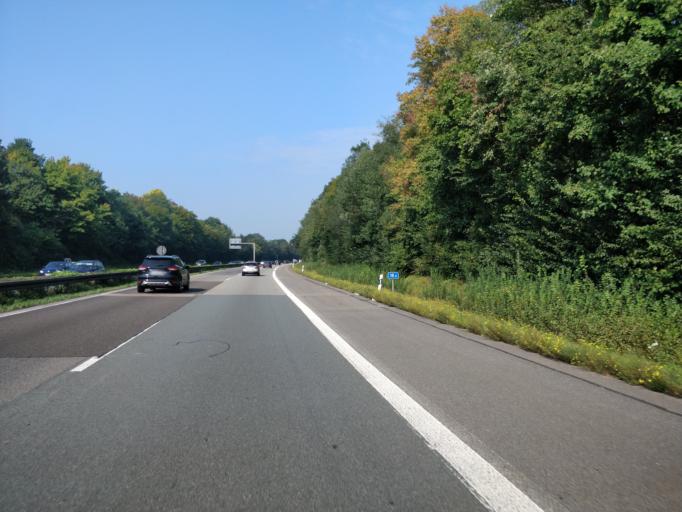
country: DE
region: North Rhine-Westphalia
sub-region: Regierungsbezirk Koln
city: Wahn-Heide
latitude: 50.8261
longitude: 7.0982
